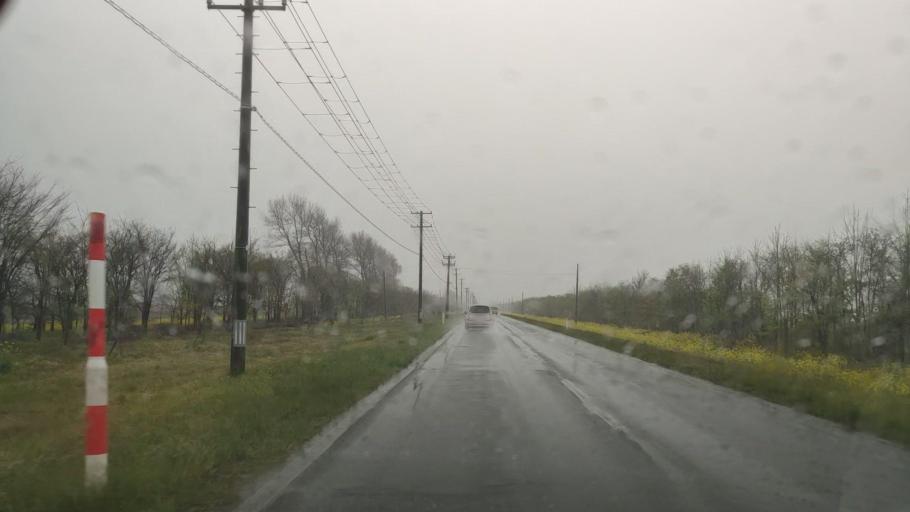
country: JP
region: Akita
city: Tenno
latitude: 39.9700
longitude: 139.9462
